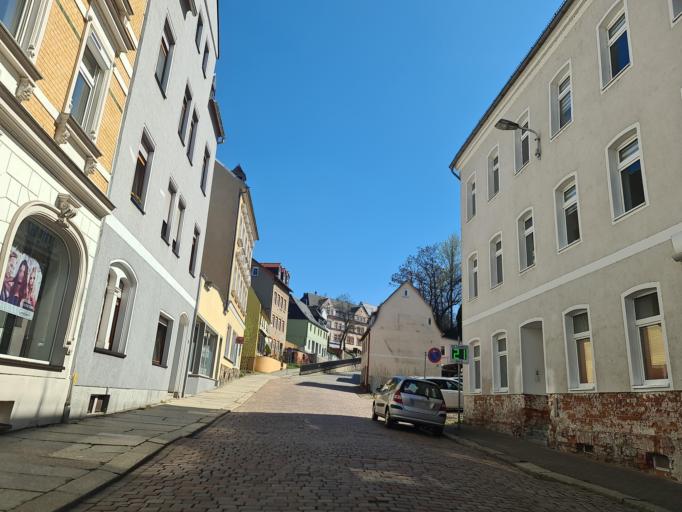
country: DE
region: Saxony
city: Glauchau
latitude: 50.8239
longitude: 12.5426
